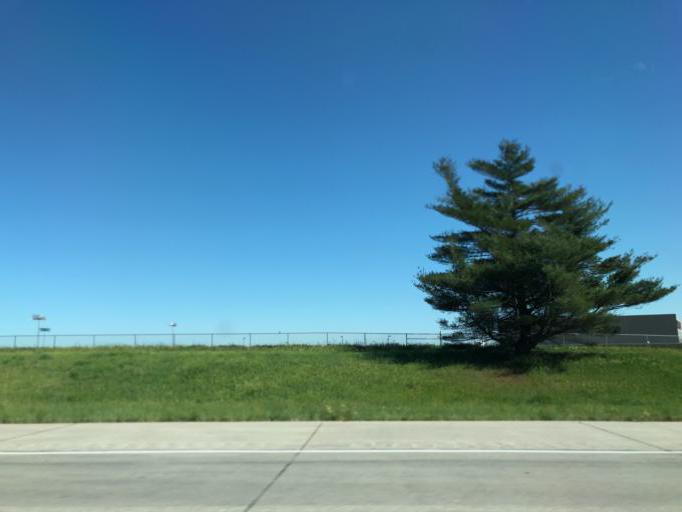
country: US
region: Nebraska
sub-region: Lancaster County
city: Waverly
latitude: 40.9024
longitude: -96.5321
